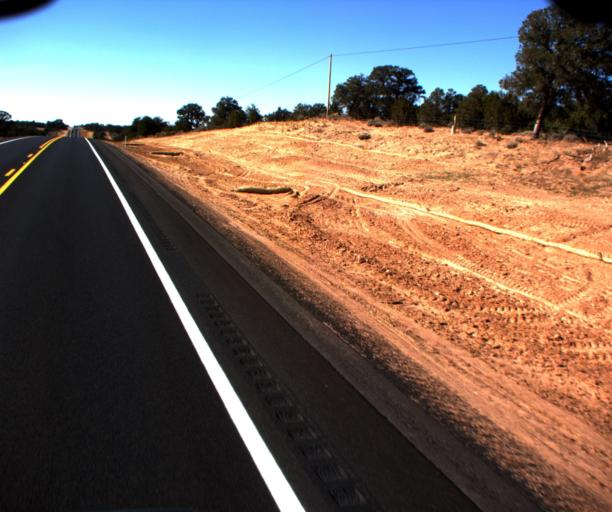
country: US
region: Arizona
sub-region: Apache County
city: Ganado
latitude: 35.7173
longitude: -109.3523
